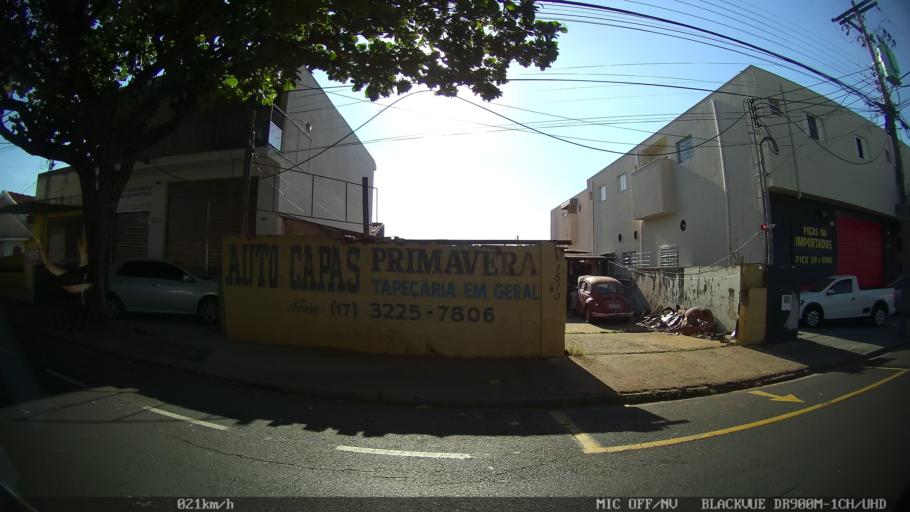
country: BR
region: Sao Paulo
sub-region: Sao Jose Do Rio Preto
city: Sao Jose do Rio Preto
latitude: -20.7939
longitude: -49.3638
